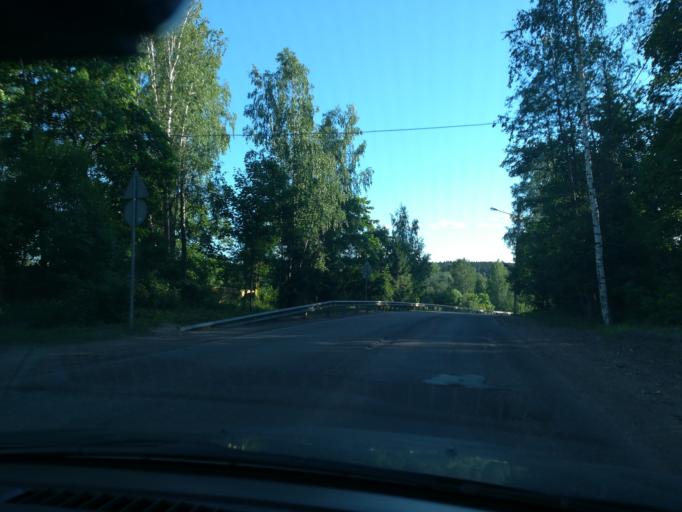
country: RU
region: Leningrad
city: Lesogorskiy
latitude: 61.0400
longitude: 28.9219
